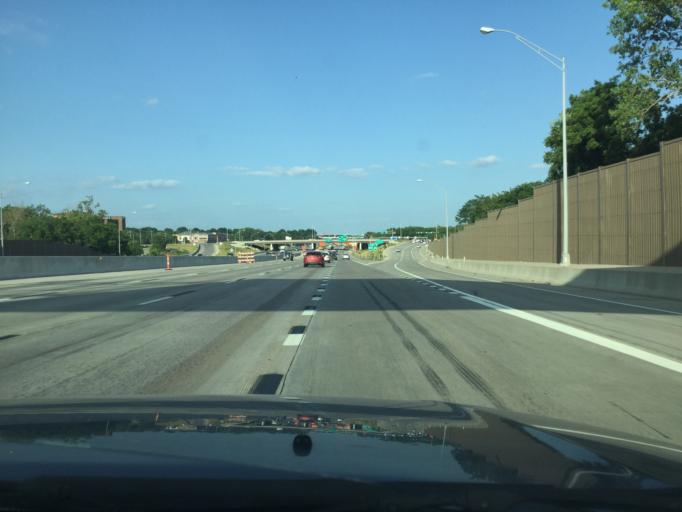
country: US
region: Kansas
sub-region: Johnson County
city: Lenexa
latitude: 38.9349
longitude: -94.7293
